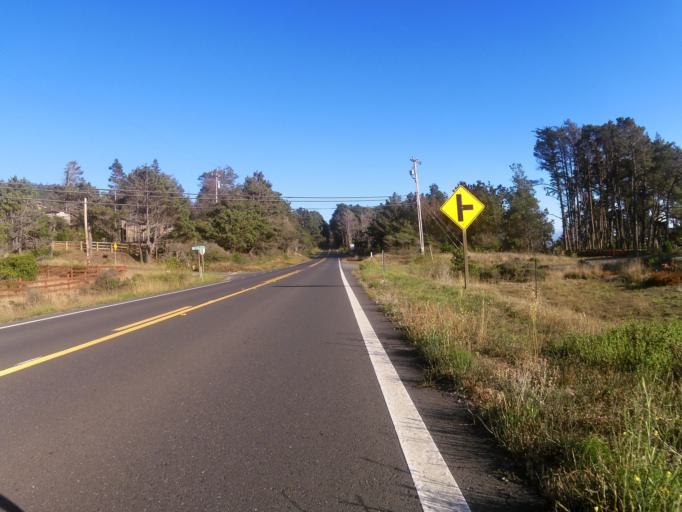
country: US
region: California
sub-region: Sonoma County
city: Sea Ranch
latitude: 38.7818
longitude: -123.5482
